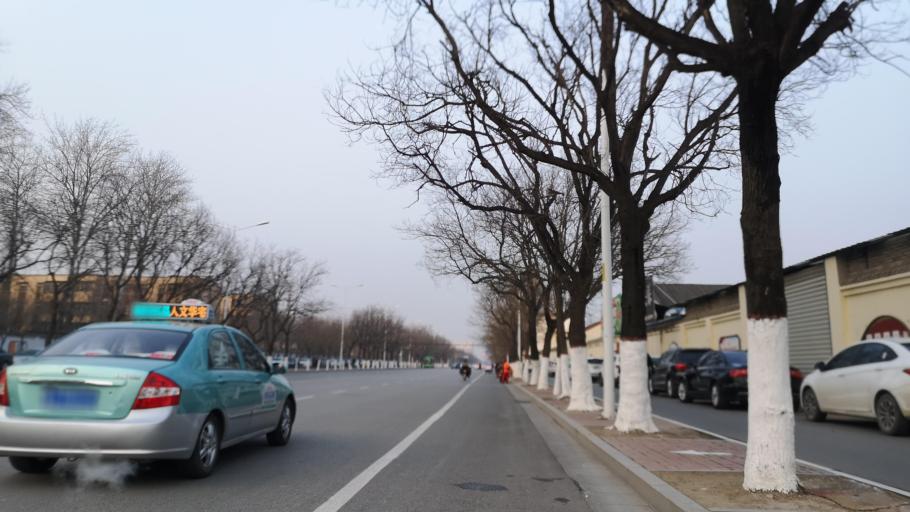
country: CN
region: Henan Sheng
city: Zhongyuanlu
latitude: 35.7653
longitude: 115.0985
